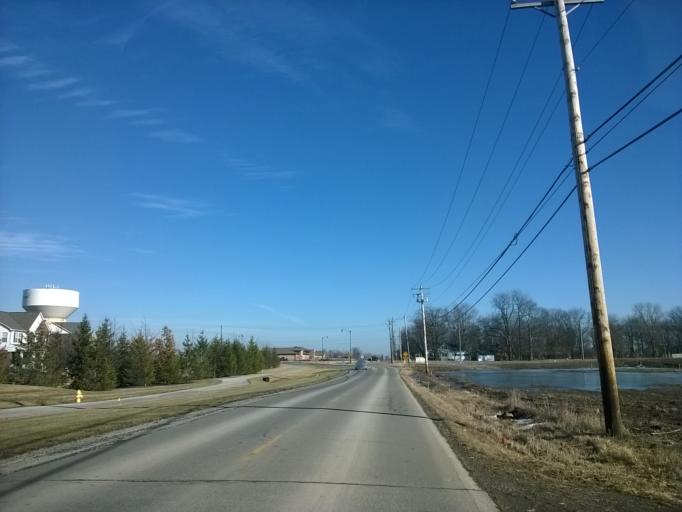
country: US
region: Indiana
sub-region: Boone County
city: Zionsville
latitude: 39.9772
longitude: -86.2241
